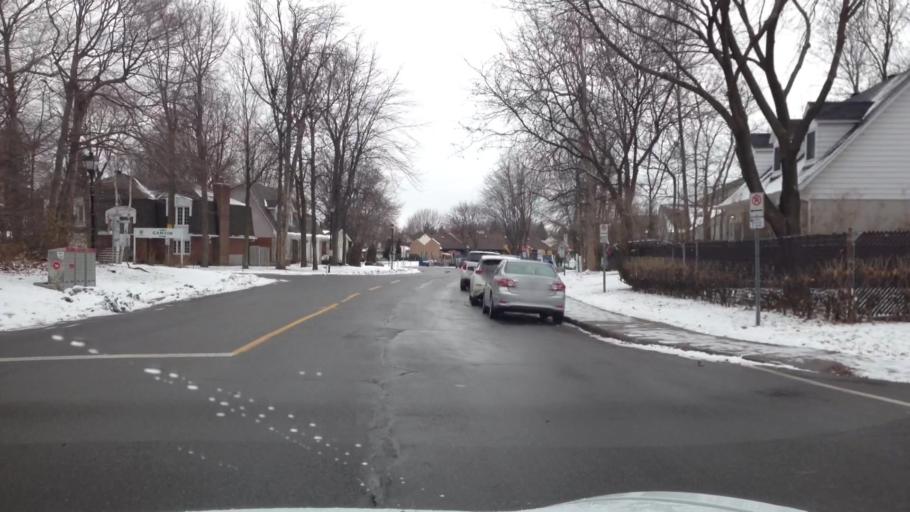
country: CA
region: Quebec
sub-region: Montreal
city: Pointe-Claire
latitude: 45.4471
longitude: -73.8361
